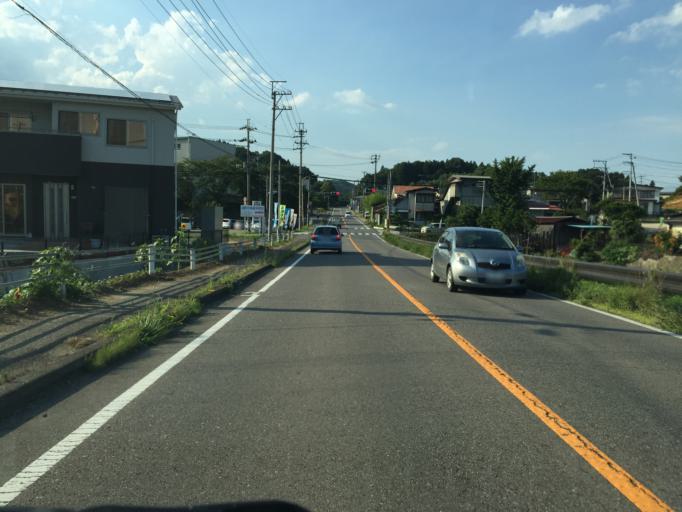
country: JP
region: Fukushima
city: Nihommatsu
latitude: 37.5780
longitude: 140.4169
